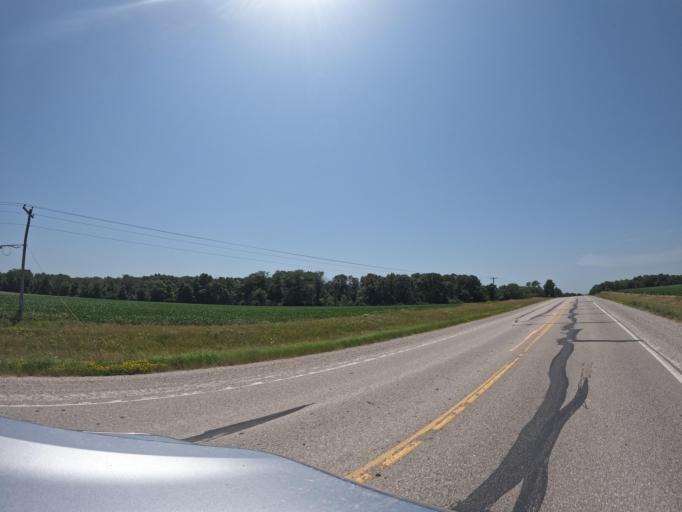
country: US
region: Iowa
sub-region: Henry County
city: Mount Pleasant
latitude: 40.9671
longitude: -91.6189
